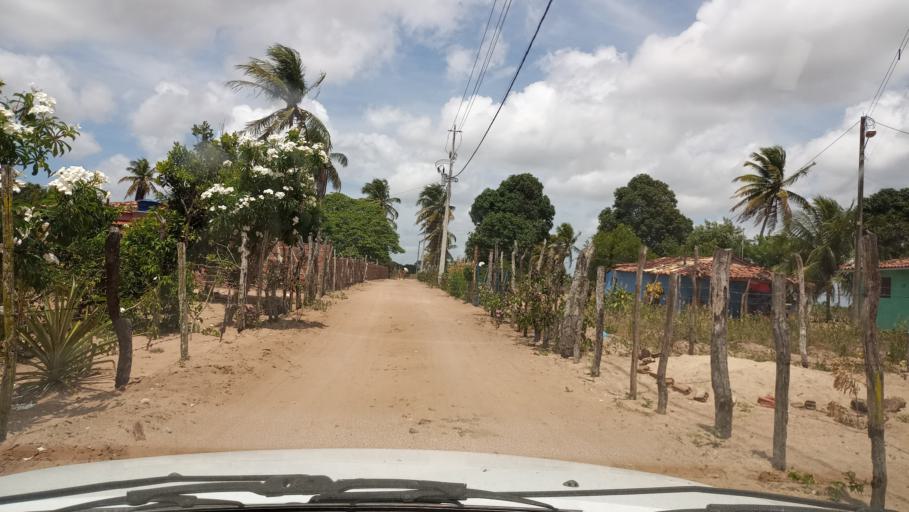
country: BR
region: Rio Grande do Norte
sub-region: Goianinha
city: Goianinha
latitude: -6.2854
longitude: -35.2837
